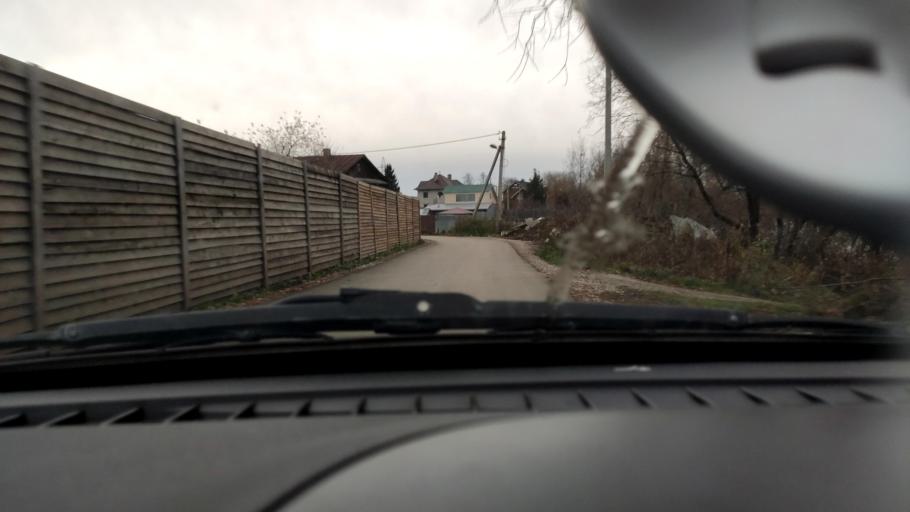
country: RU
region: Perm
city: Kondratovo
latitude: 57.9948
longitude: 56.1228
